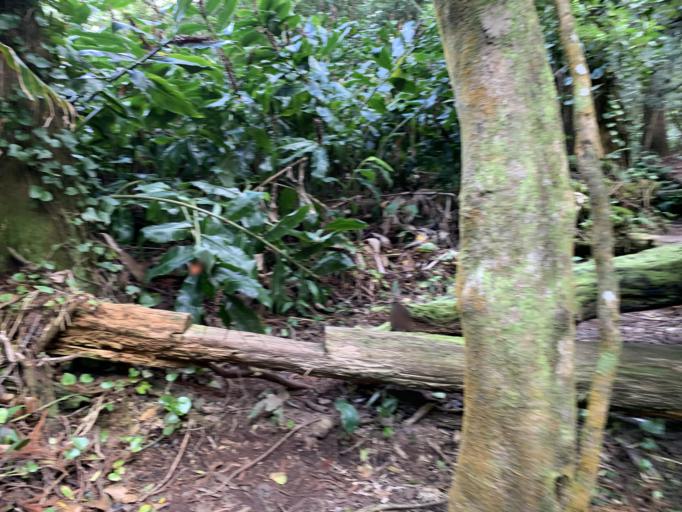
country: PT
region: Azores
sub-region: Ribeira Grande
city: Rabo de Peixe
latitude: 37.7958
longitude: -25.4905
